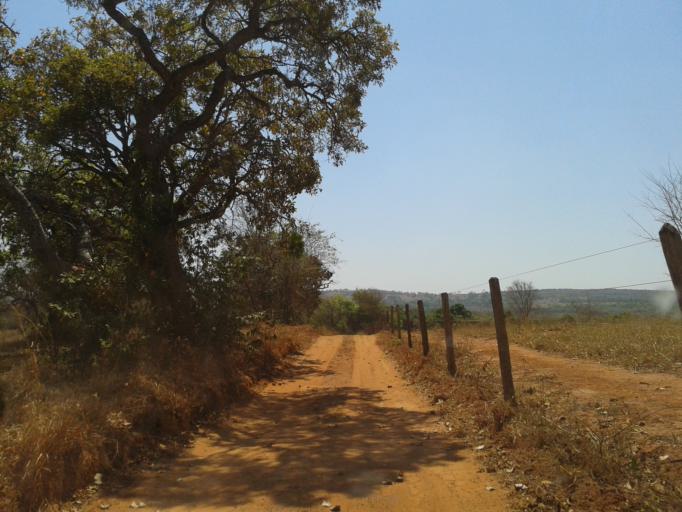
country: BR
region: Minas Gerais
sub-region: Ituiutaba
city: Ituiutaba
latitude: -19.0471
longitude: -49.3752
